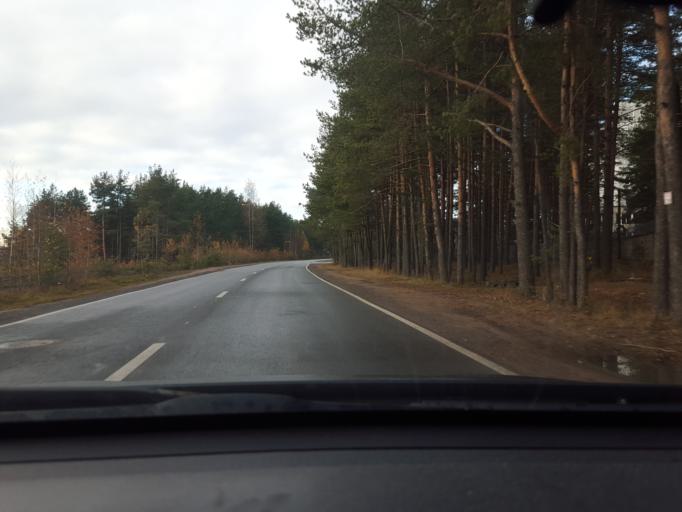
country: RU
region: St.-Petersburg
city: Kolomyagi
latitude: 60.0454
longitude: 30.2569
